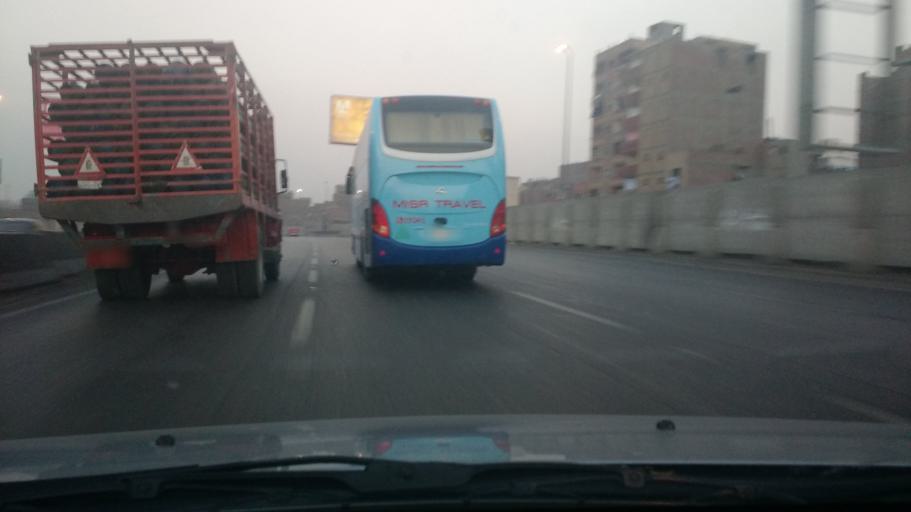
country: EG
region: Al Jizah
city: Al Jizah
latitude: 29.9902
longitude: 31.2579
